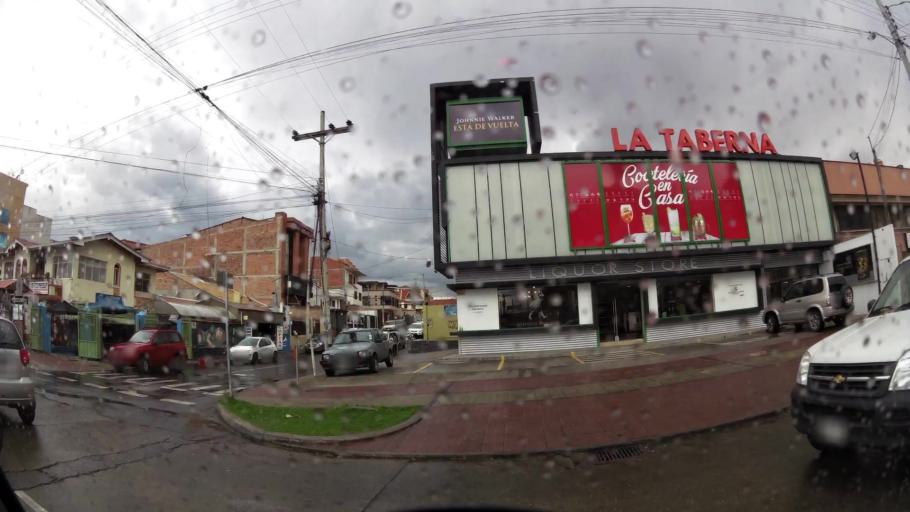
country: EC
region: Azuay
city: Cuenca
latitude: -2.9028
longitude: -79.0145
